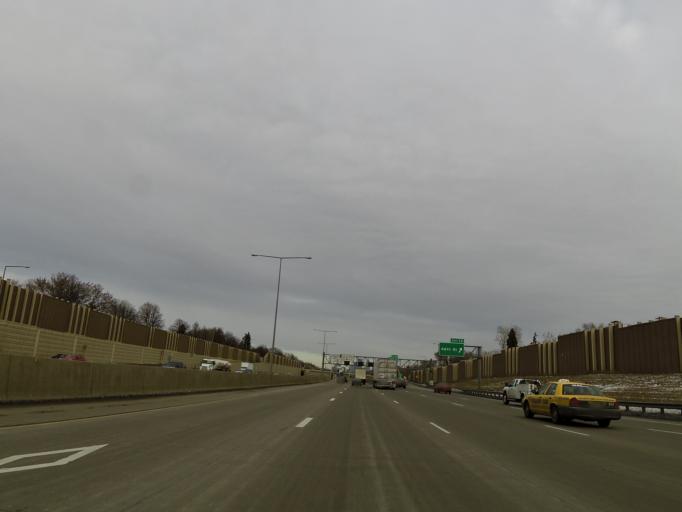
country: US
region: Minnesota
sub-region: Hennepin County
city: Richfield
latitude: 44.9152
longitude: -93.2747
